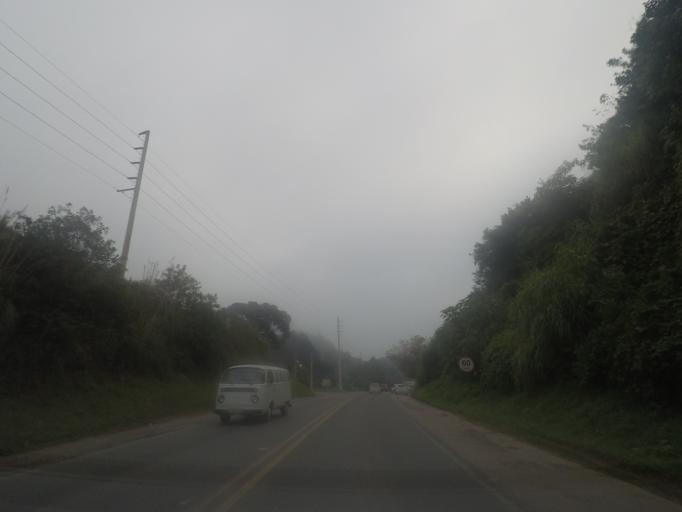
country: BR
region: Parana
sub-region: Almirante Tamandare
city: Almirante Tamandare
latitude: -25.3113
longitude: -49.3038
